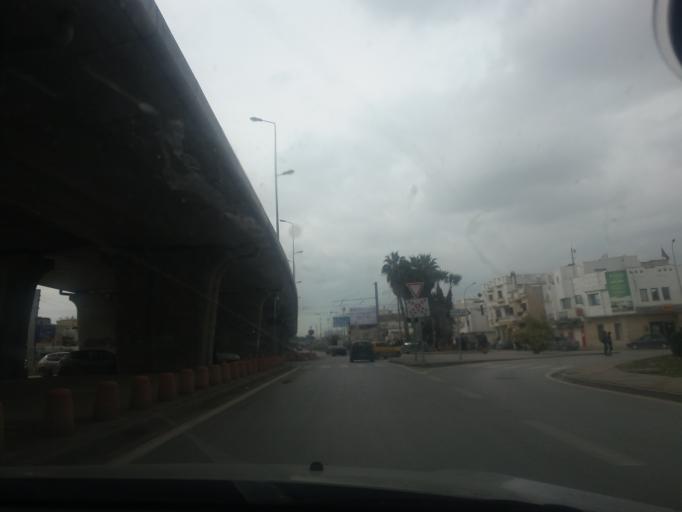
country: TN
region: Tunis
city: Tunis
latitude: 36.8283
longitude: 10.1918
